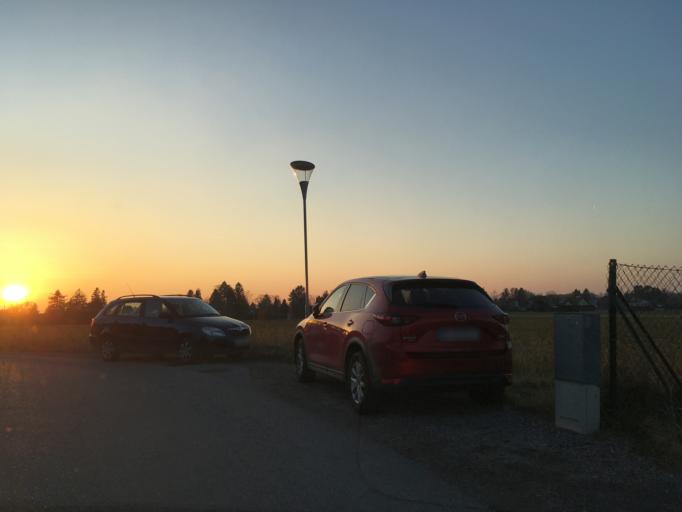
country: AT
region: Lower Austria
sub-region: Politischer Bezirk Tulln
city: Wordern
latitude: 48.3252
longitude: 16.2017
